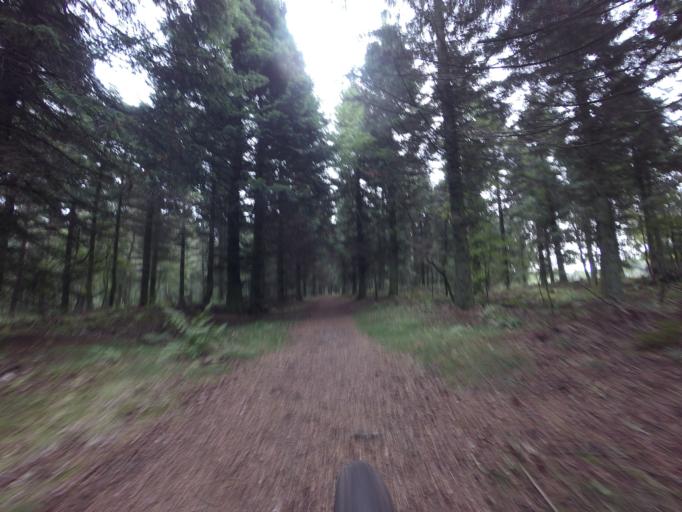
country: DK
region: North Denmark
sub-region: Hjorring Kommune
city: Hirtshals
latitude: 57.5773
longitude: 10.0472
